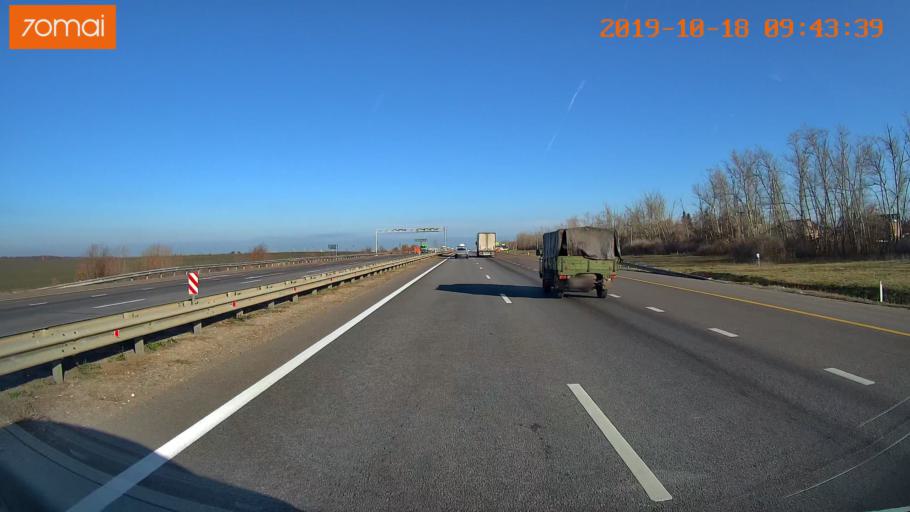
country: RU
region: Tula
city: Kazachka
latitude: 53.3007
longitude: 38.1784
